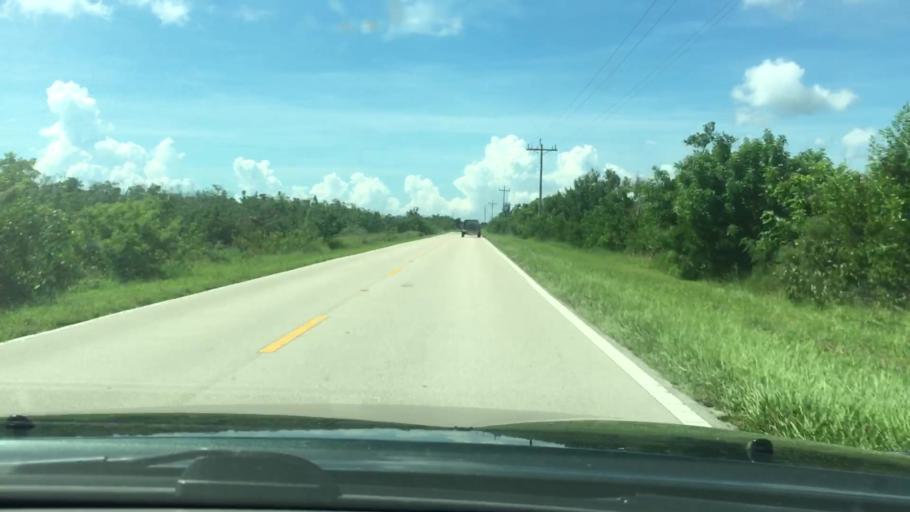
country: US
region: Florida
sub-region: Collier County
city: Marco
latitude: 25.9435
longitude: -81.6447
